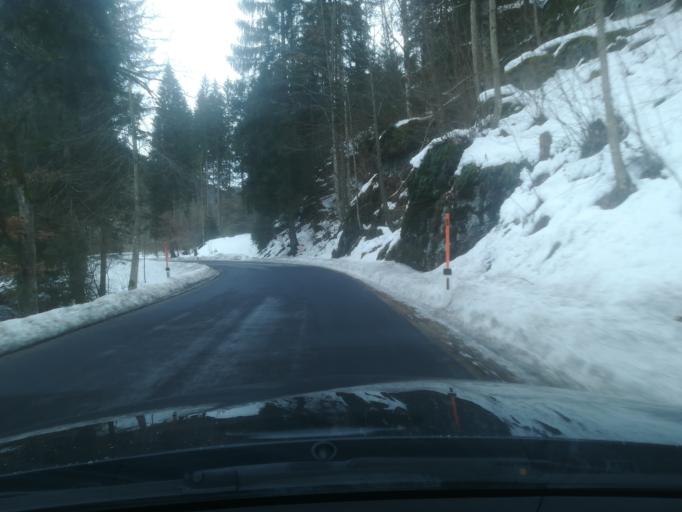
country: AT
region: Upper Austria
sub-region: Politischer Bezirk Perg
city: Perg
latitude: 48.4108
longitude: 14.6374
